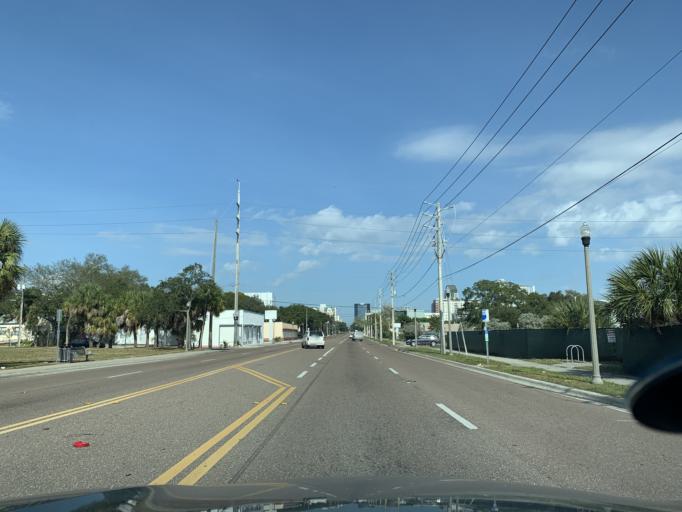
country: US
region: Florida
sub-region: Pinellas County
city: Saint Petersburg
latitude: 27.7586
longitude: -82.6384
